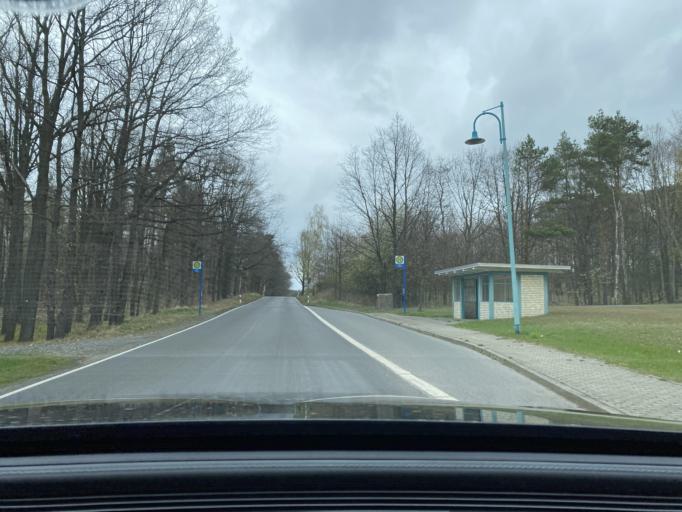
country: DE
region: Saxony
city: Puschwitz
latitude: 51.2571
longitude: 14.3011
